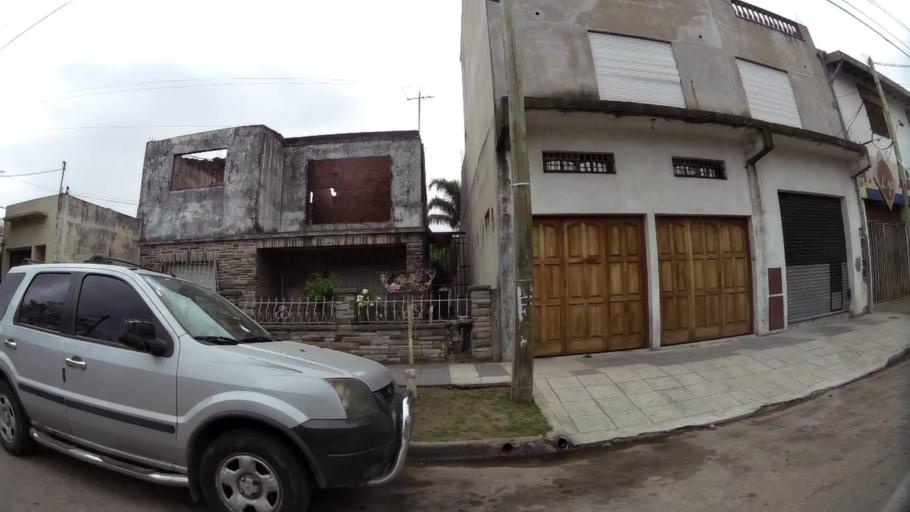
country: AR
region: Buenos Aires
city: San Justo
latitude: -34.7176
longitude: -58.5255
